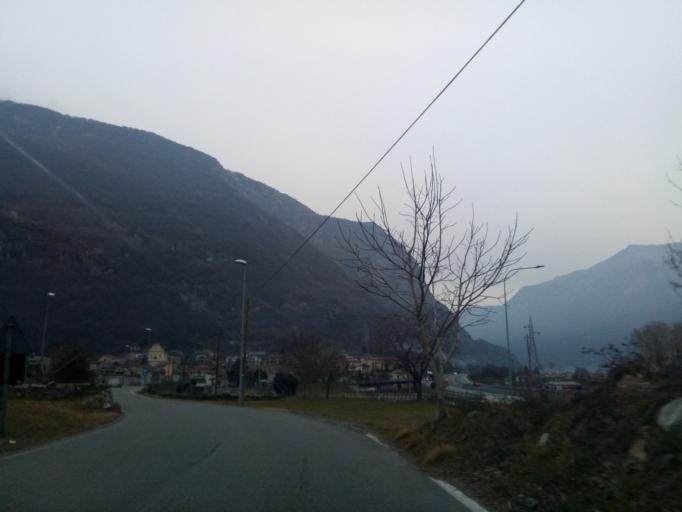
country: IT
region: Piedmont
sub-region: Provincia di Torino
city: Quincinetto
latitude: 45.5606
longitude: 7.8130
